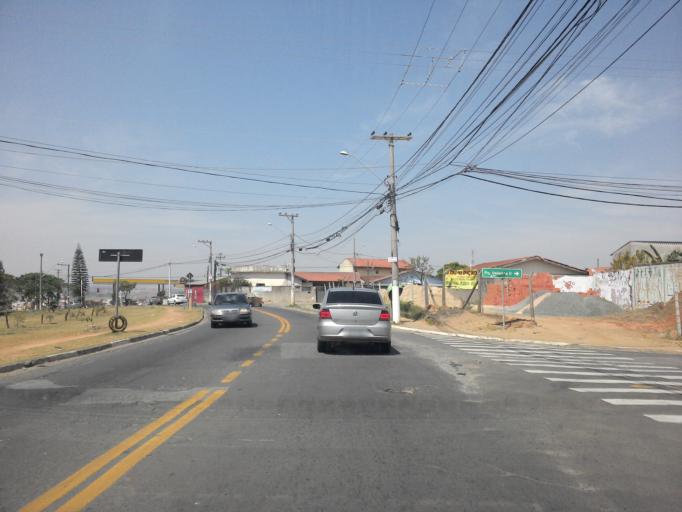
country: BR
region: Sao Paulo
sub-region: Hortolandia
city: Hortolandia
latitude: -22.9415
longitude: -47.1833
